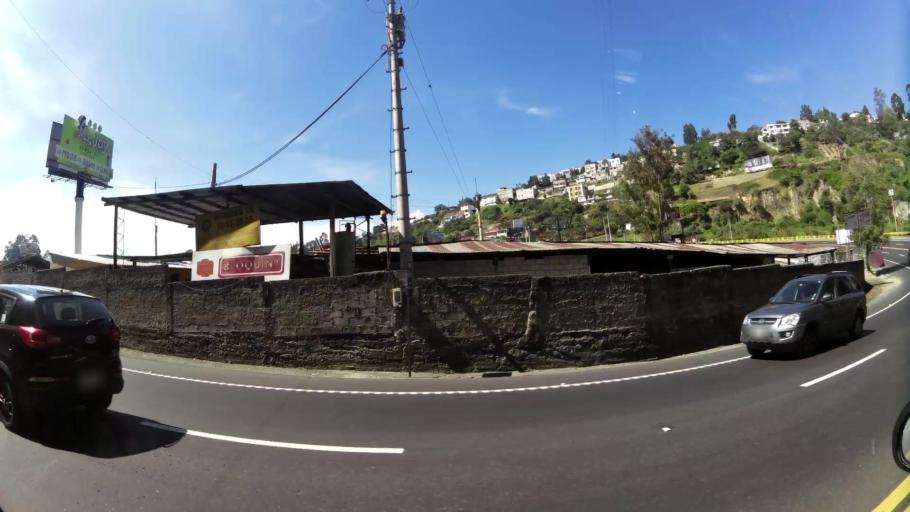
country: EC
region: Pichincha
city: Quito
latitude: -0.1937
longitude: -78.4457
